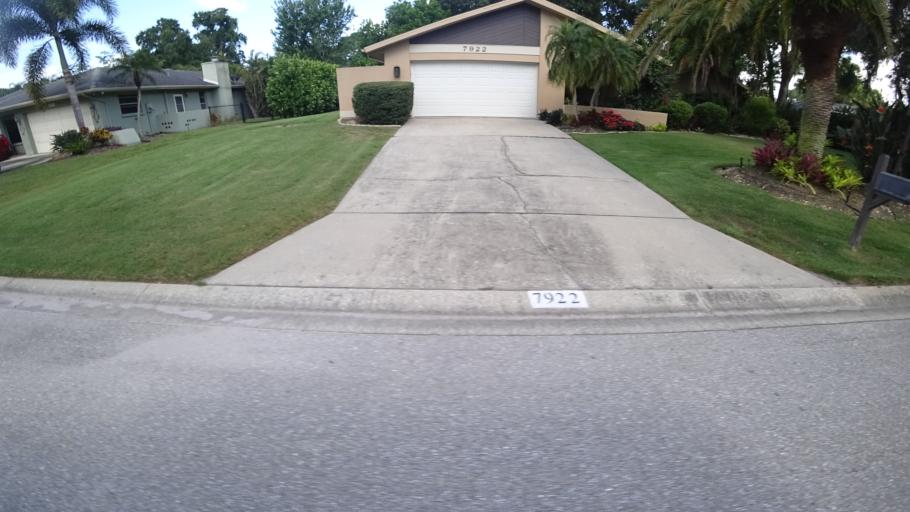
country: US
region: Florida
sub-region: Sarasota County
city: Desoto Lakes
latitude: 27.3981
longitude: -82.4937
